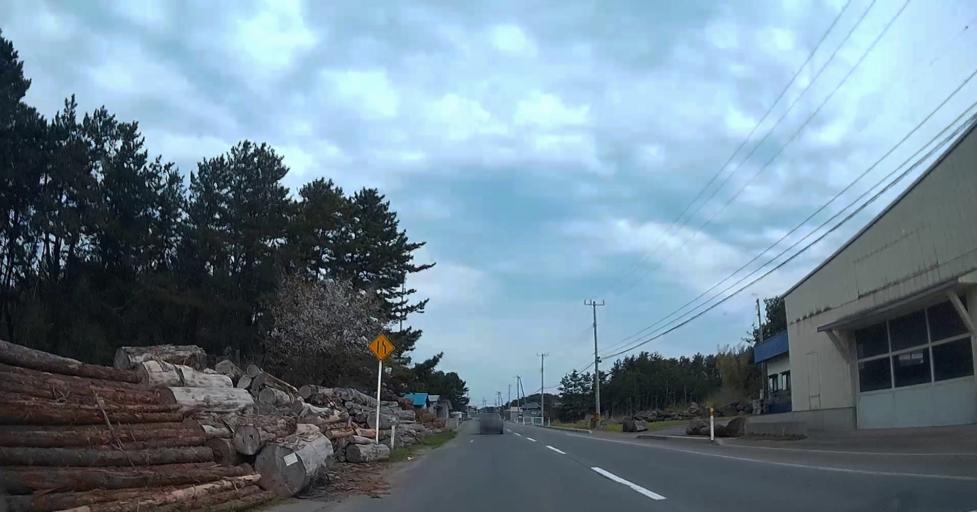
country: JP
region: Aomori
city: Shimokizukuri
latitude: 41.0225
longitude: 140.3305
